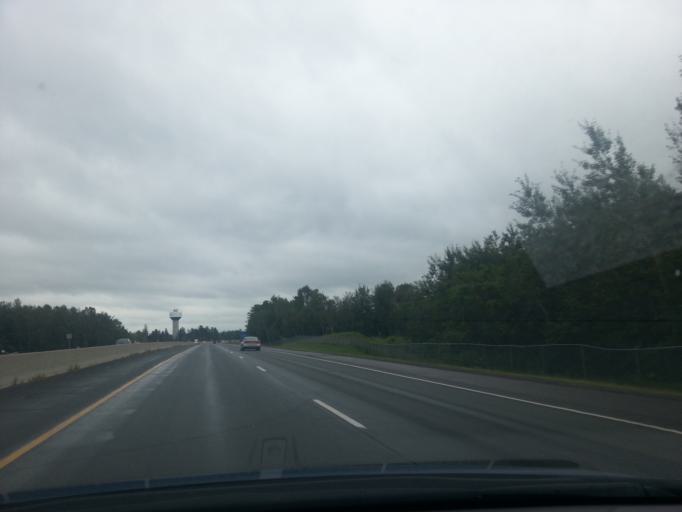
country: CA
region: New Brunswick
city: Oromocto
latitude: 45.8416
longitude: -66.5049
